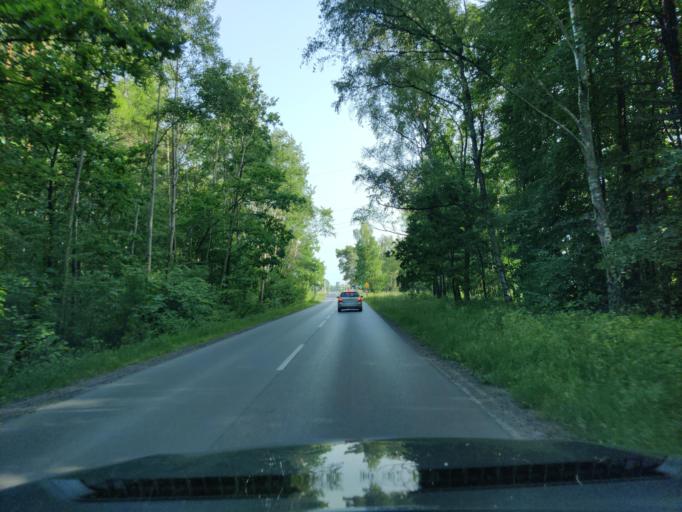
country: PL
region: Masovian Voivodeship
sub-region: Powiat wyszkowski
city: Wyszkow
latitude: 52.6229
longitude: 21.4520
